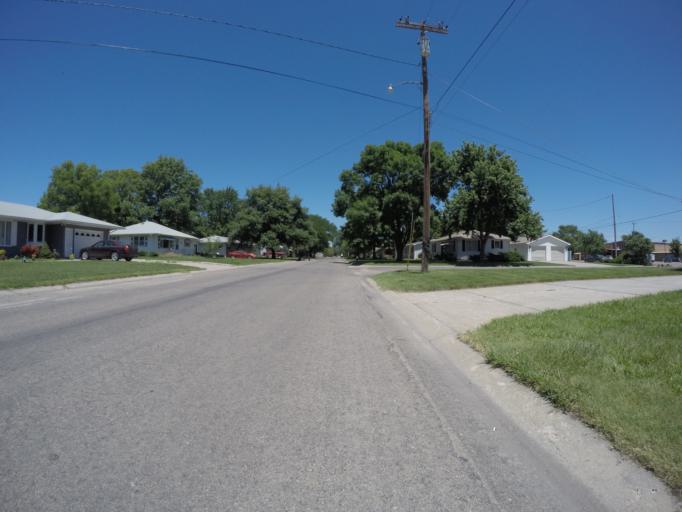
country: US
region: Kansas
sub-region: Republic County
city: Belleville
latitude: 39.8169
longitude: -97.6282
